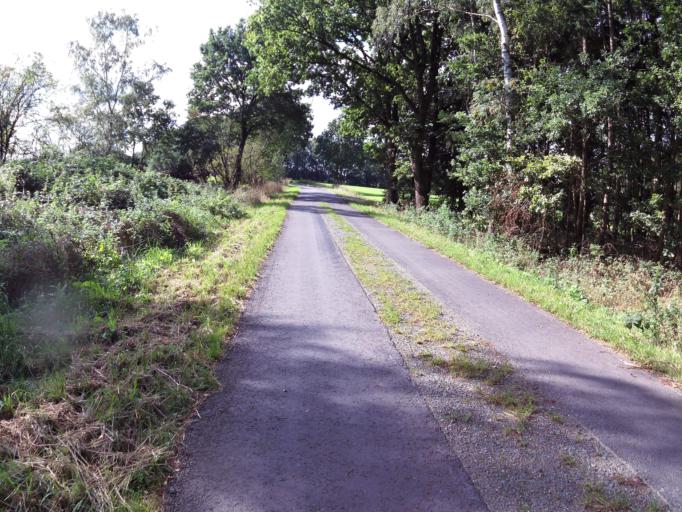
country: DE
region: Lower Saxony
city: Sandbostel
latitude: 53.4458
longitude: 9.1241
